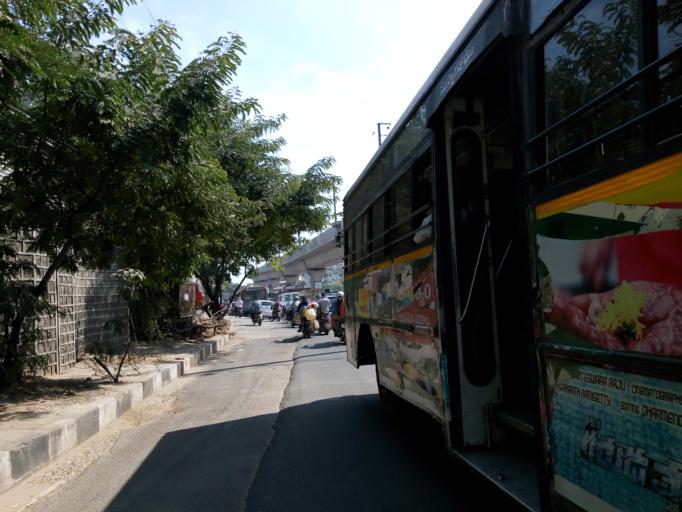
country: IN
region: Telangana
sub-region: Rangareddi
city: Uppal Kalan
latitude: 17.4227
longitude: 78.5380
